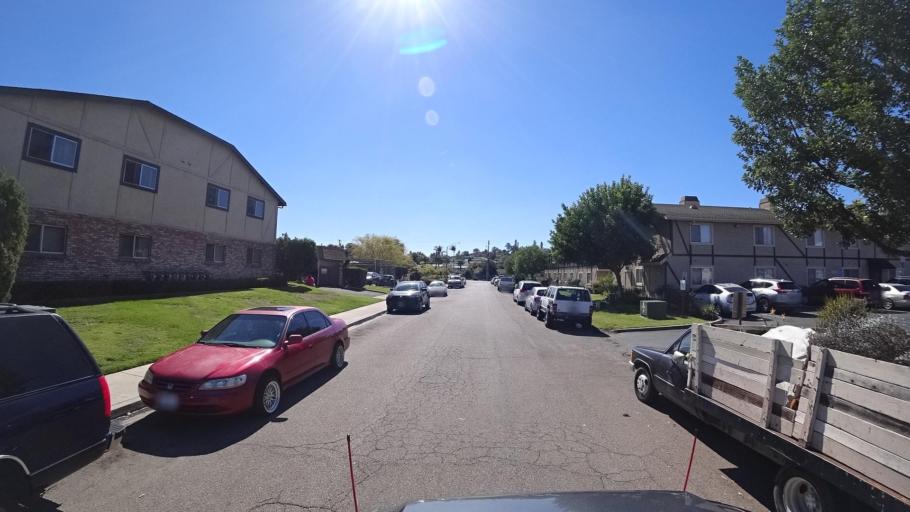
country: US
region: California
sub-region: San Diego County
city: Winter Gardens
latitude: 32.8219
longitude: -116.9319
